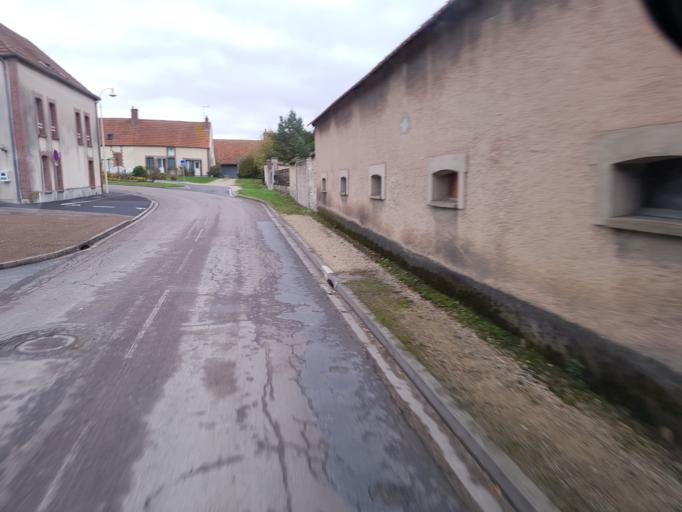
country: FR
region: Champagne-Ardenne
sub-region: Departement de la Marne
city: Saint-Just-Sauvage
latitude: 48.5815
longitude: 3.8540
